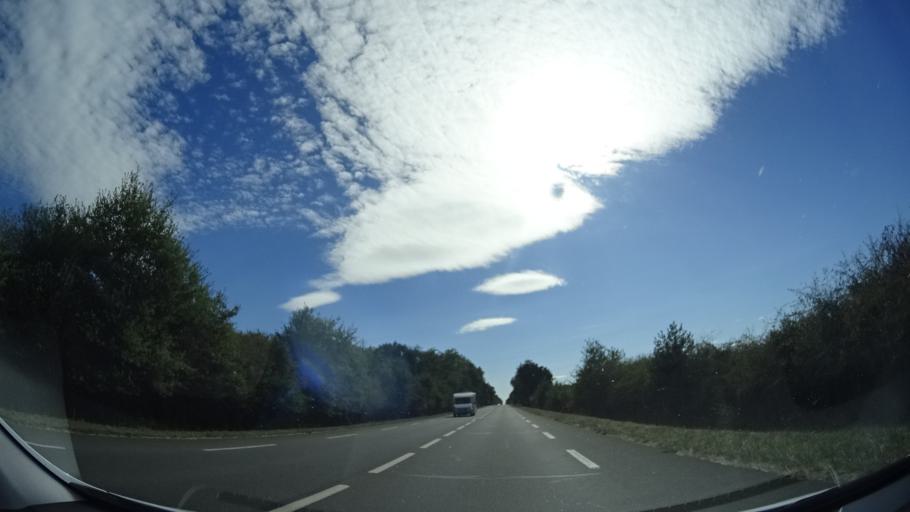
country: FR
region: Centre
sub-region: Departement du Loiret
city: Vitry-aux-Loges
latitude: 47.9390
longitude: 2.3540
